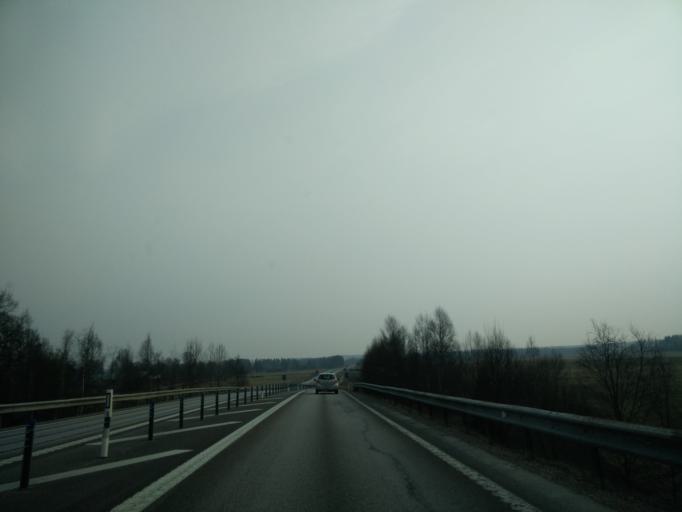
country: SE
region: Vaermland
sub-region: Forshaga Kommun
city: Forshaga
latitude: 59.4423
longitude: 13.4158
